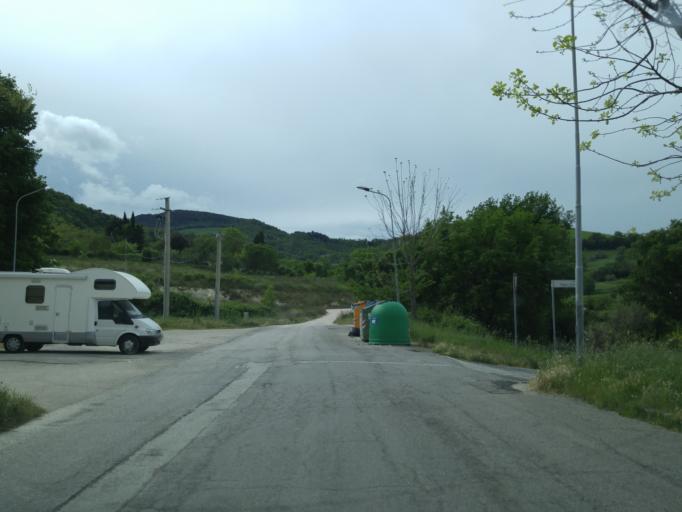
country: IT
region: The Marches
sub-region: Provincia di Pesaro e Urbino
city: Fossombrone
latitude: 43.6993
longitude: 12.8167
